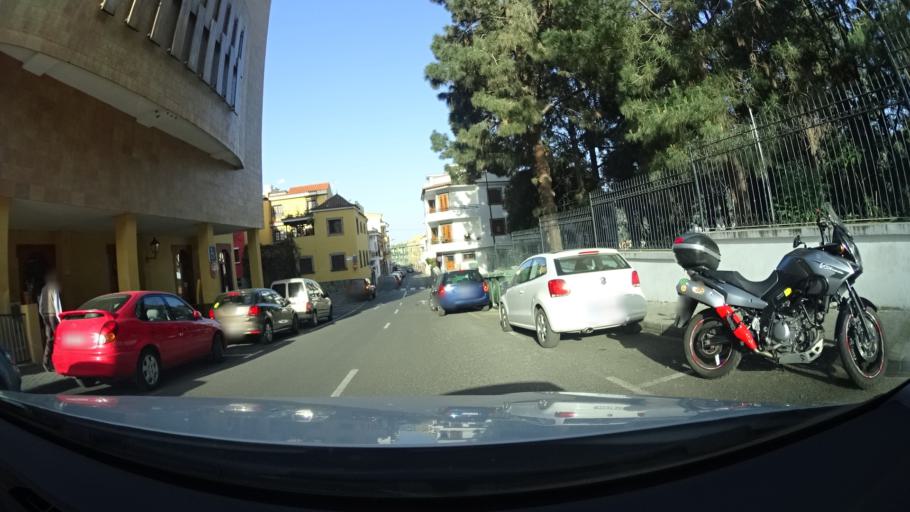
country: ES
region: Canary Islands
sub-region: Provincia de Las Palmas
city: Teror
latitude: 28.0584
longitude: -15.5474
